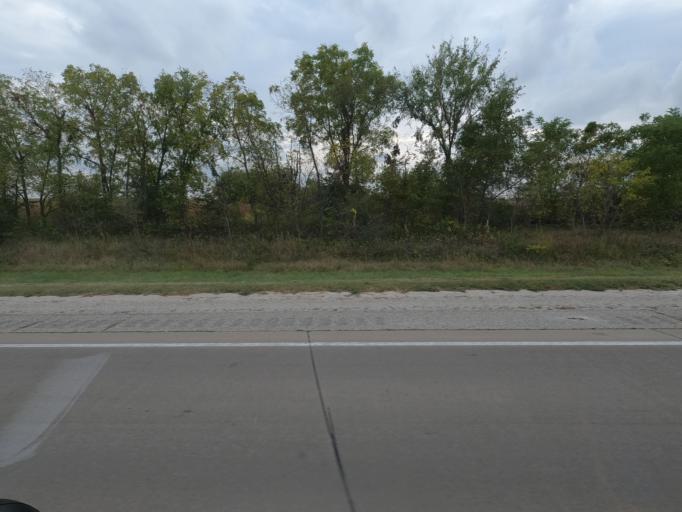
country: US
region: Iowa
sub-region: Wapello County
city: Eddyville
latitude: 41.0988
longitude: -92.5212
